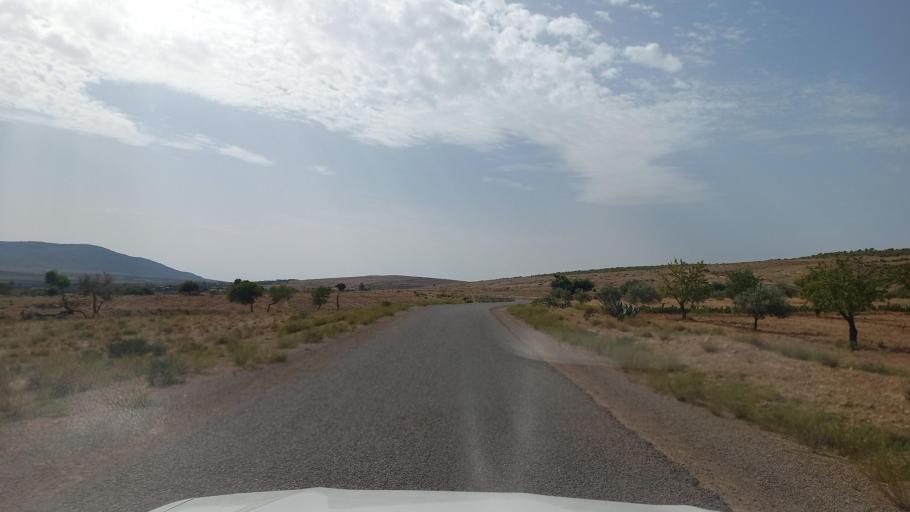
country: TN
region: Al Qasrayn
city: Kasserine
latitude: 35.3683
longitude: 8.8651
